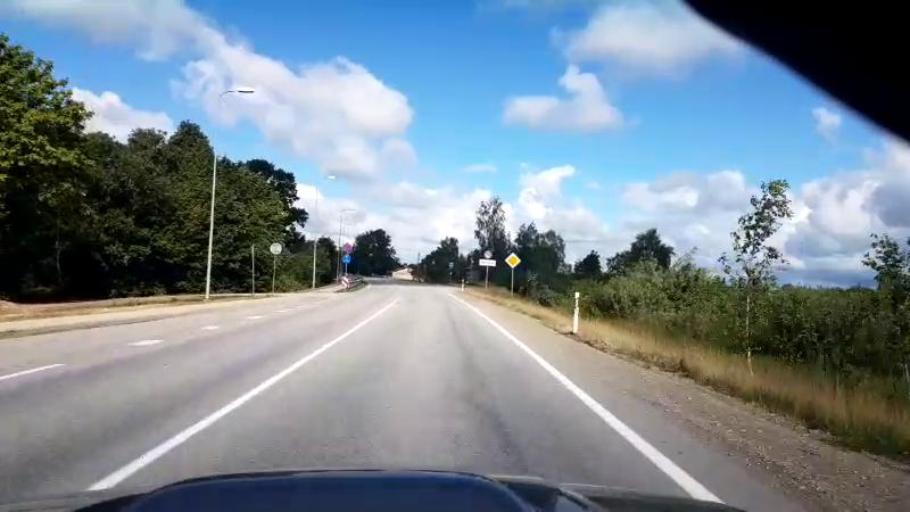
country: LV
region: Bauskas Rajons
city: Bauska
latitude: 56.4031
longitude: 24.2193
